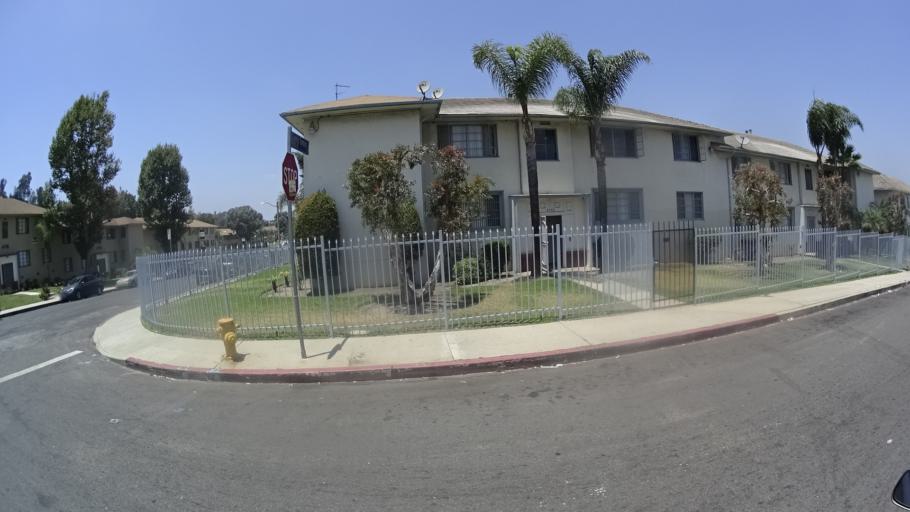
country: US
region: California
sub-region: Los Angeles County
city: View Park-Windsor Hills
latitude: 34.0100
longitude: -118.3444
